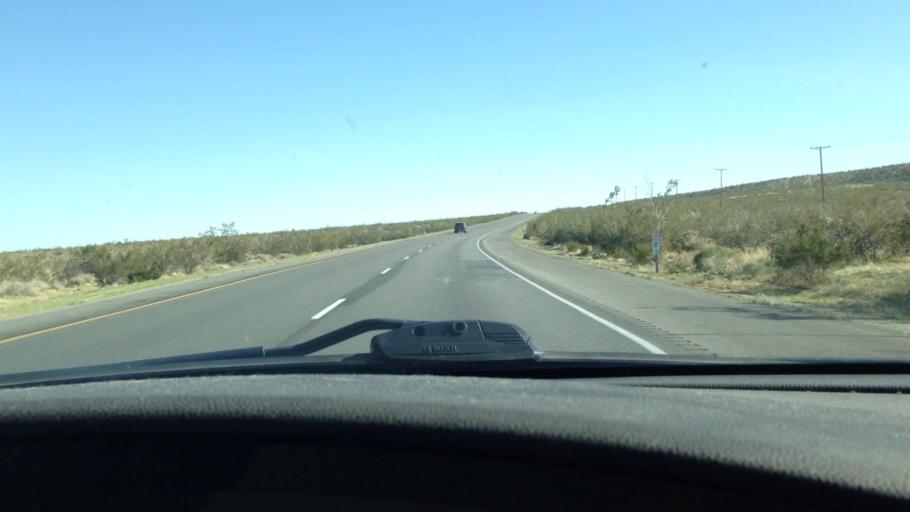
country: US
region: California
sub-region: Kern County
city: Inyokern
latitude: 35.8821
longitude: -117.8915
